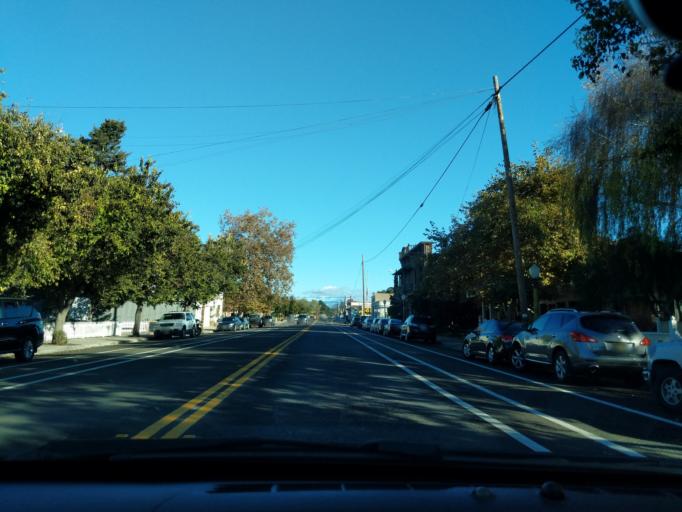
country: US
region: California
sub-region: Santa Barbara County
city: Los Alamos
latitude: 34.7441
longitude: -120.2810
